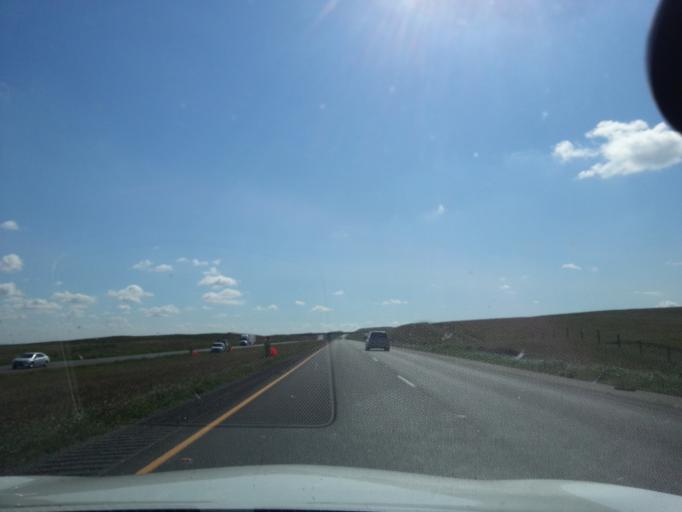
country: US
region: California
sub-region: Fresno County
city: Coalinga
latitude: 36.3359
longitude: -120.3051
